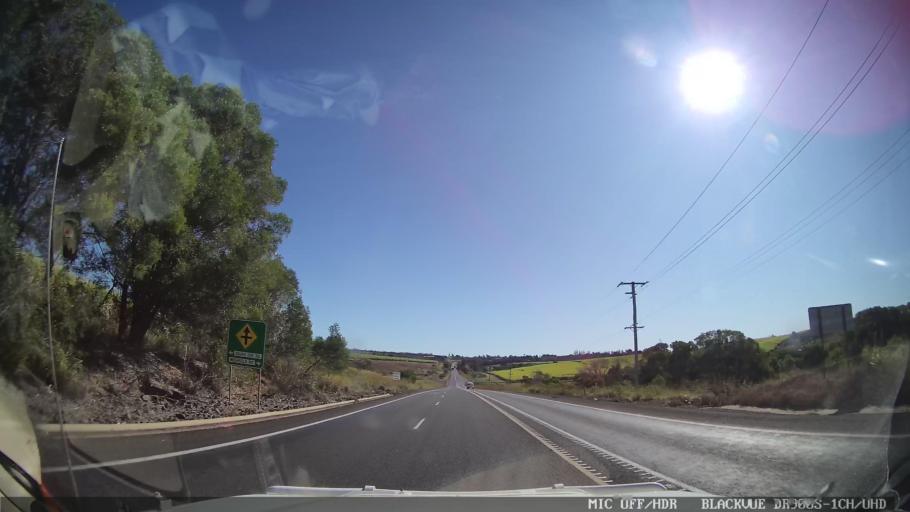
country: AU
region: Queensland
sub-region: Bundaberg
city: Childers
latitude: -25.2455
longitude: 152.3127
